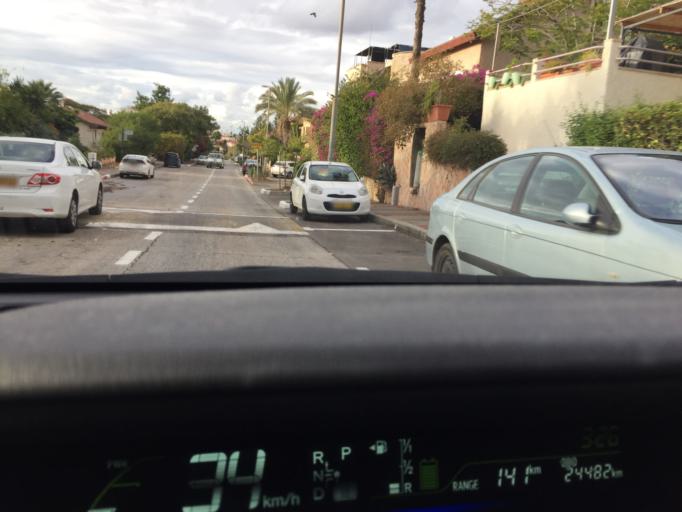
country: PS
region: West Bank
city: Az Zawiyah
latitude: 32.1093
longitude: 35.0322
